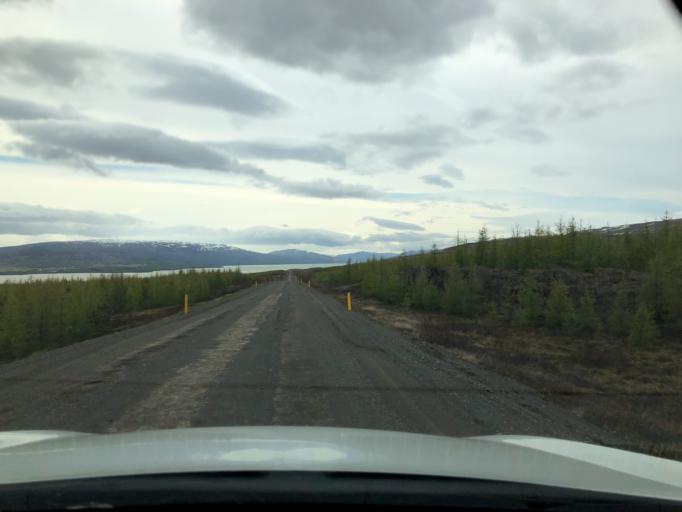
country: IS
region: East
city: Egilsstadir
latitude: 65.1999
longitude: -14.6183
